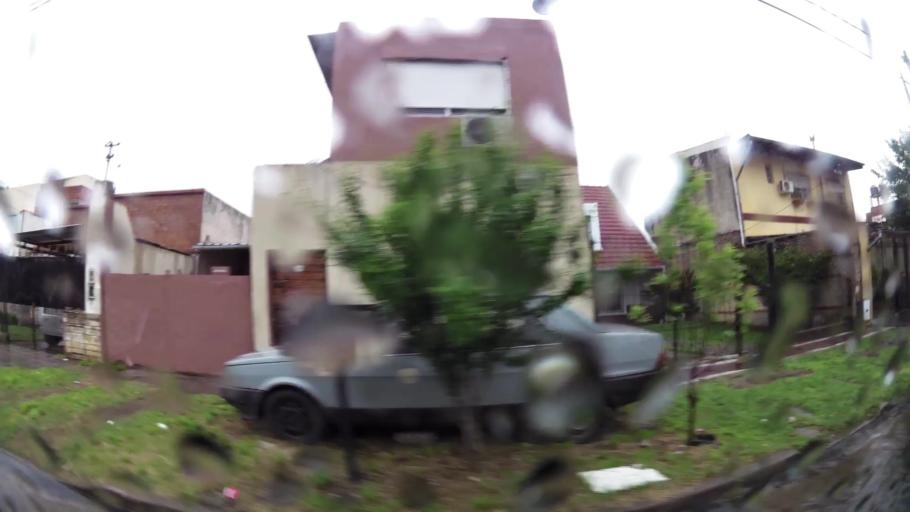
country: AR
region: Buenos Aires
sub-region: Partido de Lanus
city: Lanus
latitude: -34.7080
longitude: -58.4135
